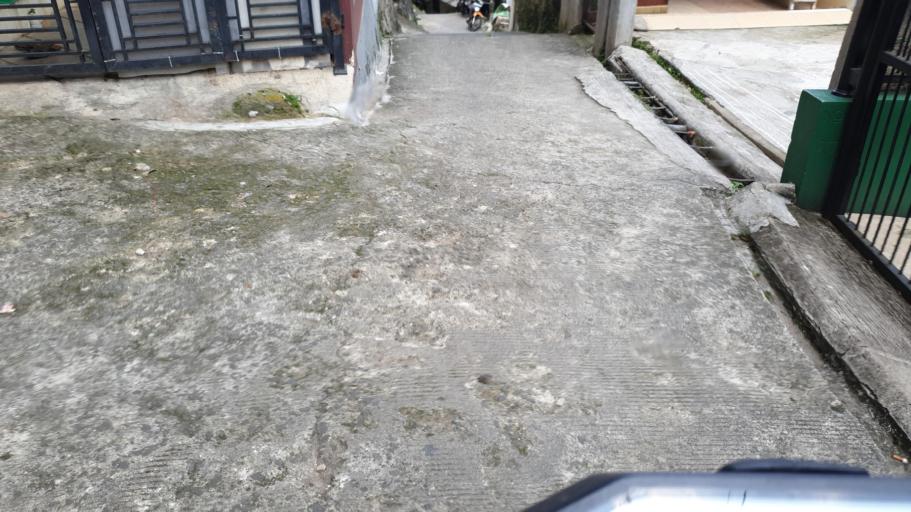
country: ID
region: West Java
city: Depok
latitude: -6.3690
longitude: 106.8383
